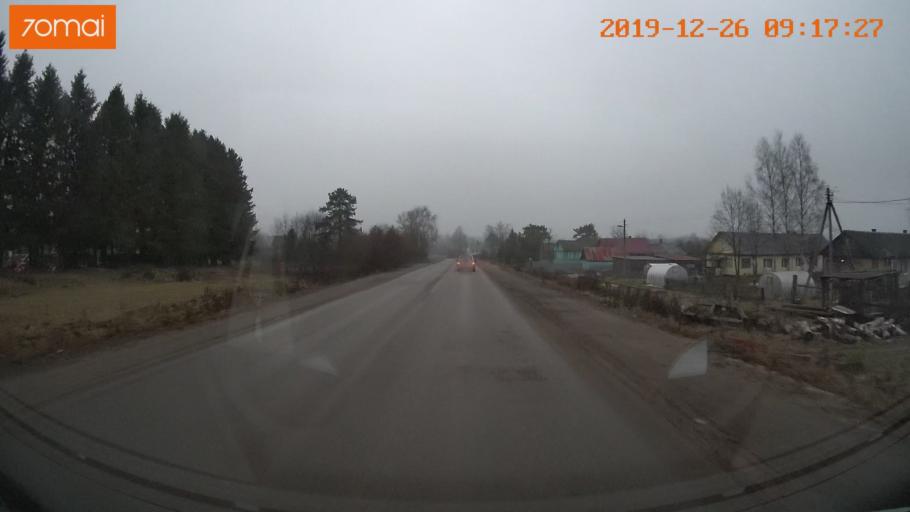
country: RU
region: Vologda
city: Gryazovets
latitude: 58.9299
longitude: 40.2394
